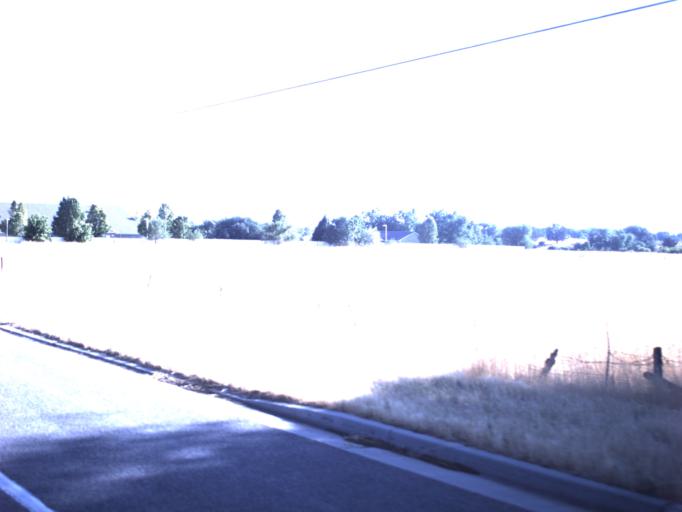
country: US
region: Utah
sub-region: Utah County
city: Mapleton
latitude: 40.1365
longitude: -111.5980
